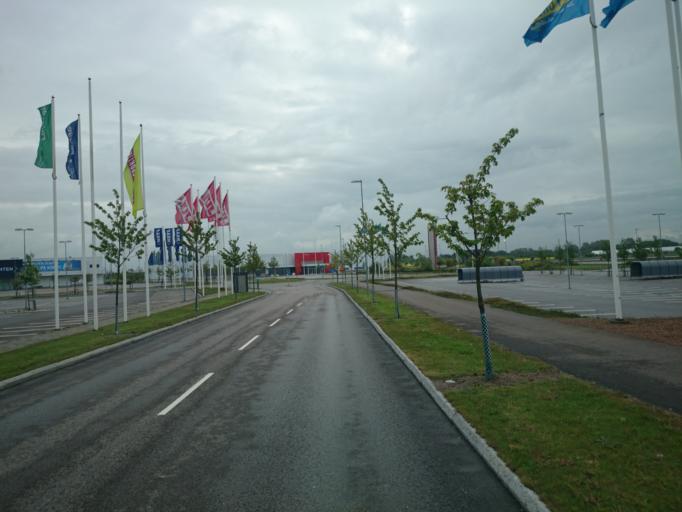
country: SE
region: Skane
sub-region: Burlovs Kommun
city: Arloev
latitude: 55.6126
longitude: 13.1018
